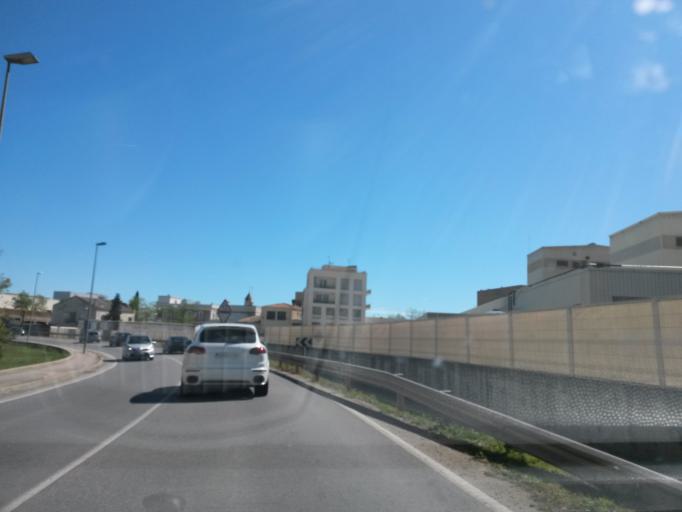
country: ES
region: Catalonia
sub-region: Provincia de Girona
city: Riudellots de la Selva
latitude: 41.8955
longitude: 2.8095
